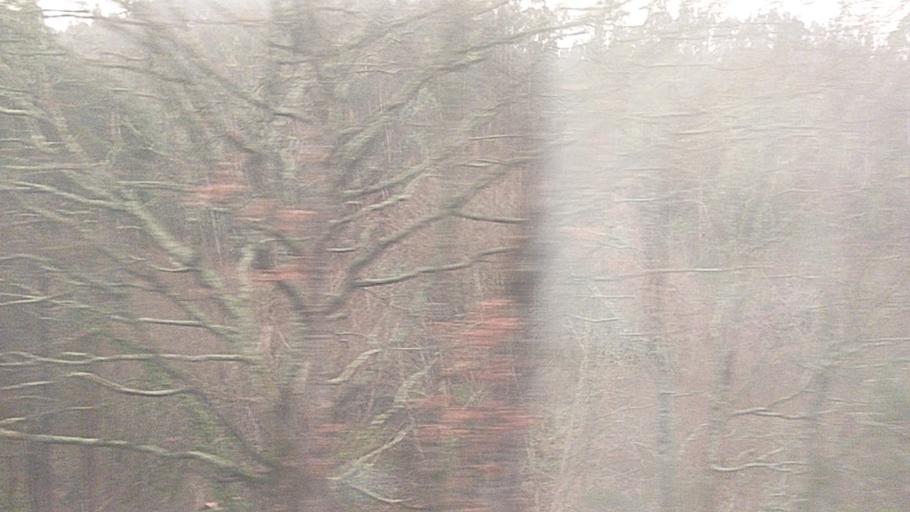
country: PT
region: Viseu
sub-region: Mortagua
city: Mortagua
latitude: 40.4079
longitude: -8.3153
